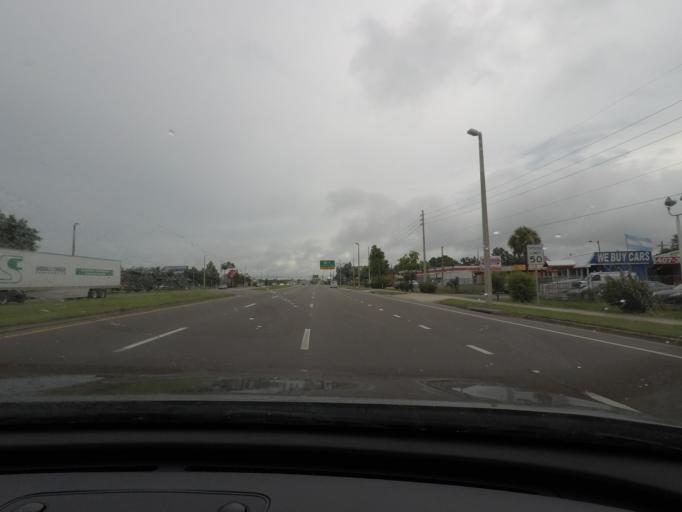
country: US
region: Florida
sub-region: Orange County
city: Union Park
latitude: 28.5618
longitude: -81.3046
